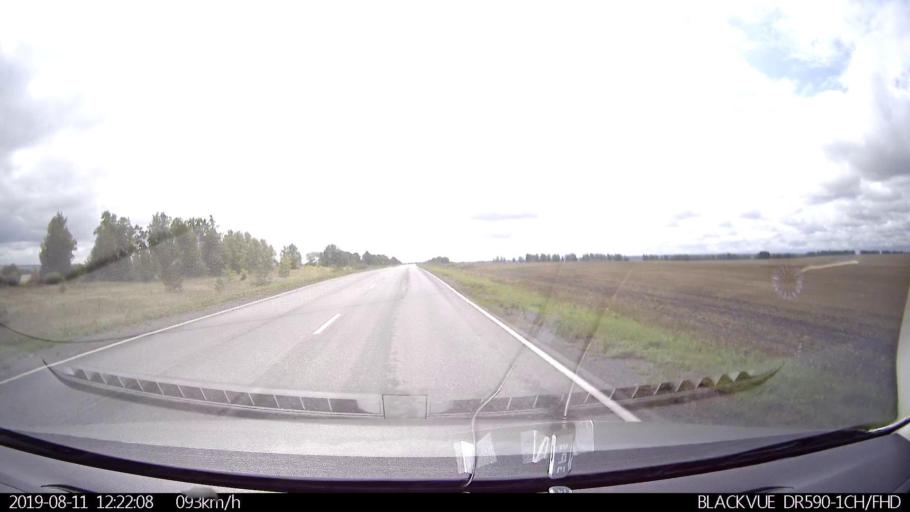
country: RU
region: Ulyanovsk
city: Ignatovka
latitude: 53.9118
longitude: 47.9552
